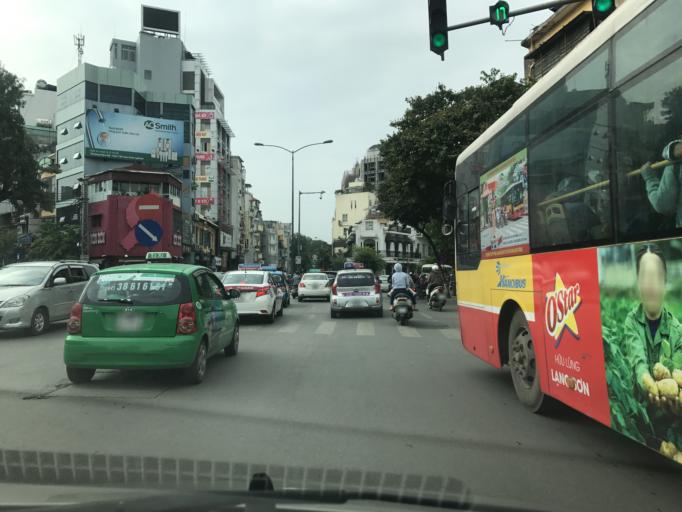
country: VN
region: Ha Noi
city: Hanoi
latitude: 21.0283
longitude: 105.8437
